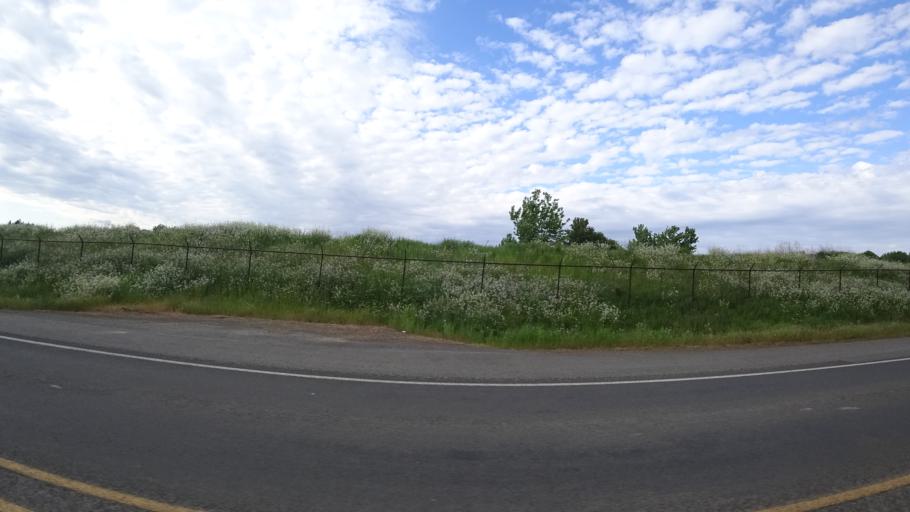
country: US
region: Oregon
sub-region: Washington County
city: Hillsboro
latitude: 45.4868
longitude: -122.9786
